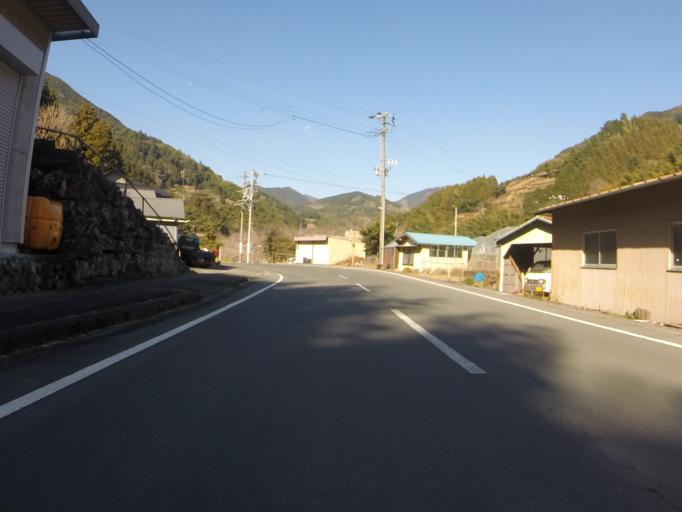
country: JP
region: Shizuoka
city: Fujinomiya
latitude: 35.1324
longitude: 138.4722
